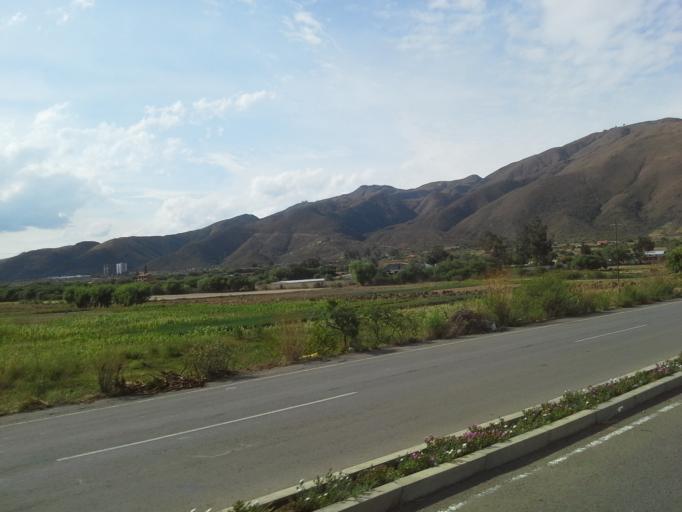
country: BO
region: Cochabamba
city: Tarata
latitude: -17.5483
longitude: -66.0063
